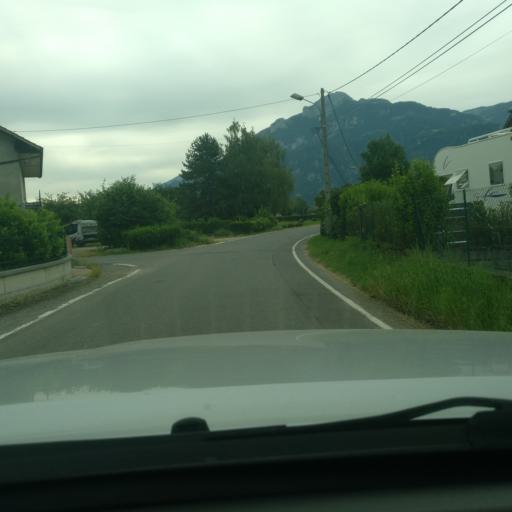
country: FR
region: Rhone-Alpes
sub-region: Departement de la Haute-Savoie
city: Amancy
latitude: 46.0789
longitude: 6.3558
